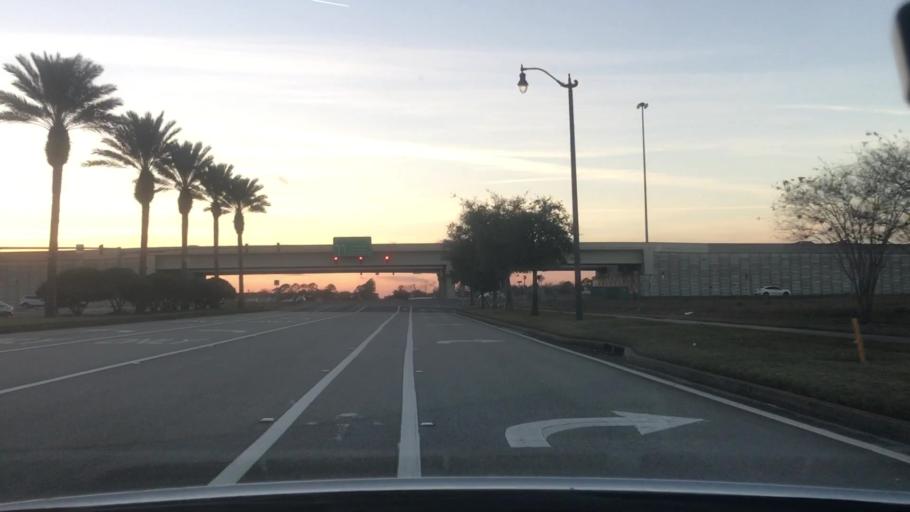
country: US
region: Florida
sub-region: Duval County
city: Jacksonville
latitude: 30.3382
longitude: -81.5507
